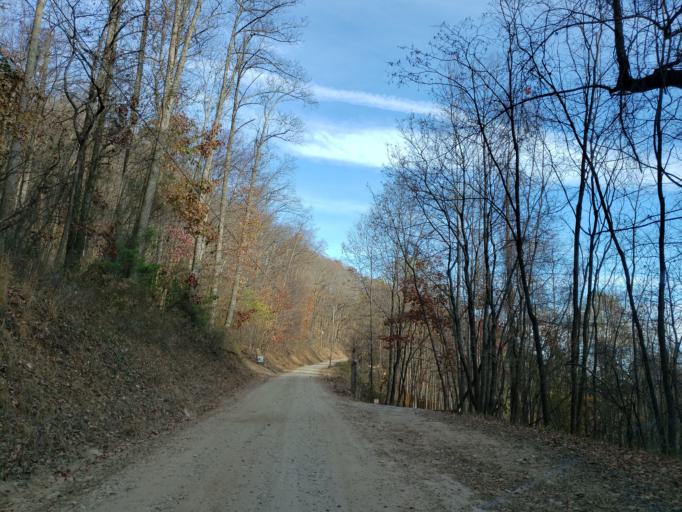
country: US
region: Georgia
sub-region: Lumpkin County
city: Dahlonega
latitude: 34.6473
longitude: -84.0889
